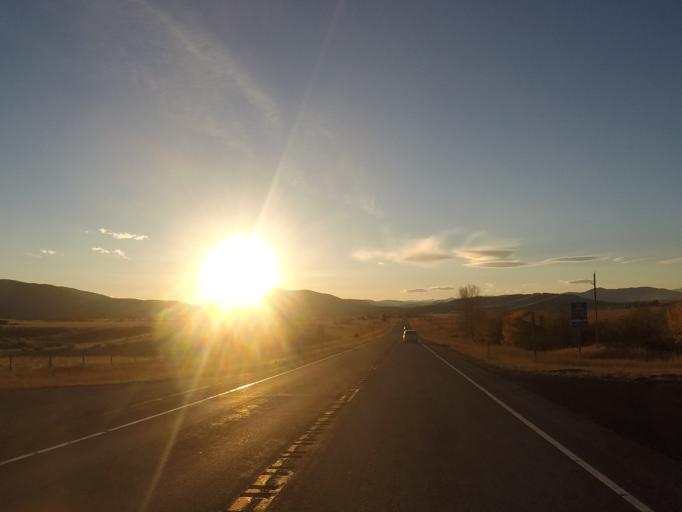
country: US
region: Montana
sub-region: Missoula County
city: Seeley Lake
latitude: 47.0201
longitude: -113.1049
